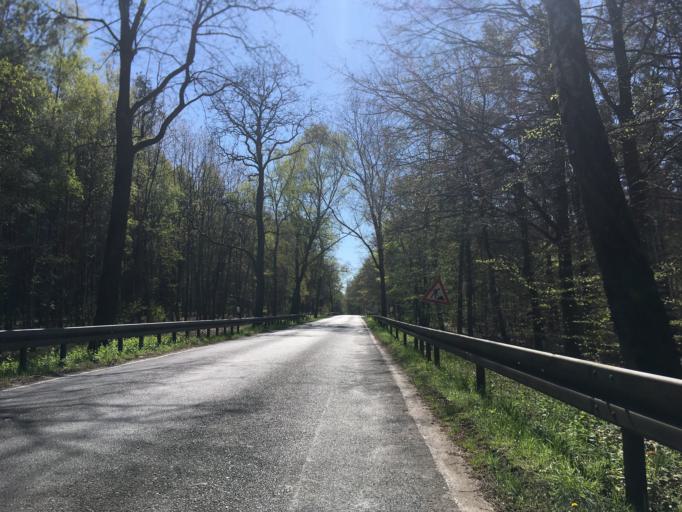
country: DE
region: Brandenburg
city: Bernau bei Berlin
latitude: 52.7157
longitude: 13.5753
